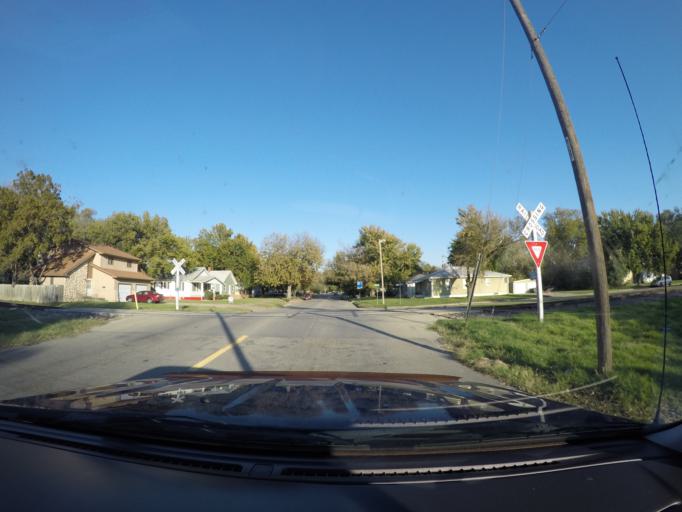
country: US
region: Kansas
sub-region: Saline County
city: Salina
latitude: 38.8417
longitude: -97.6216
